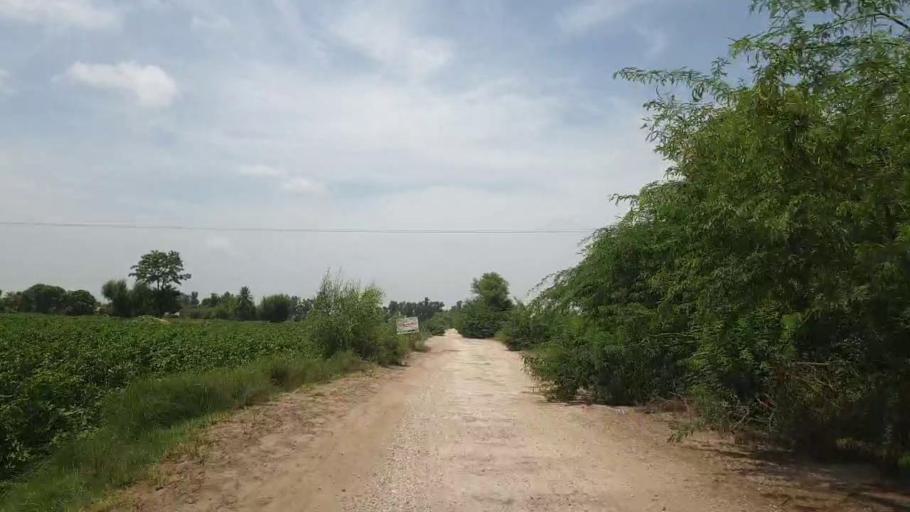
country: PK
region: Sindh
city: Kot Diji
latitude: 27.1280
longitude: 69.0029
